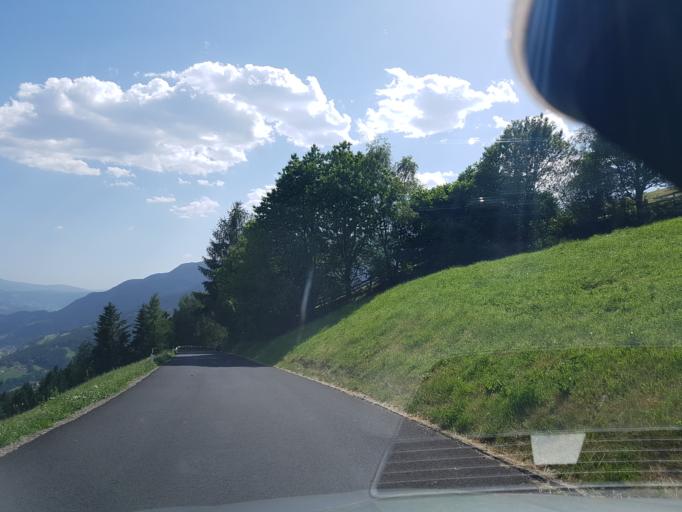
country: IT
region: Trentino-Alto Adige
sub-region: Bolzano
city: Villandro - Villanders
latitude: 46.6449
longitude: 11.5356
